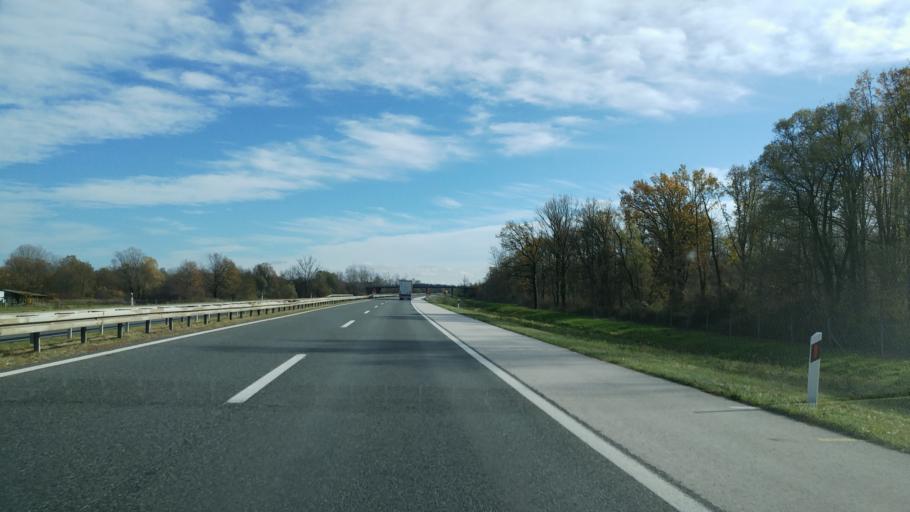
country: HR
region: Sisacko-Moslavacka
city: Husain
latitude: 45.4455
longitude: 16.8134
